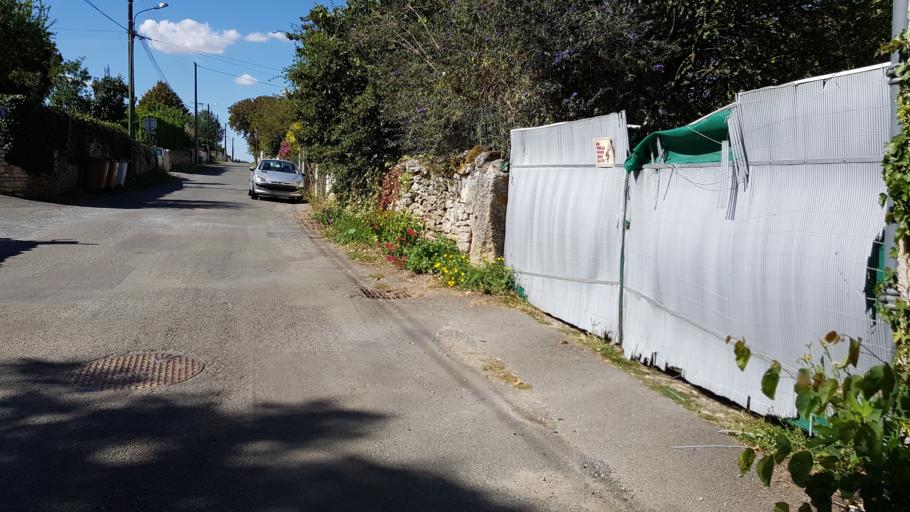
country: FR
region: Poitou-Charentes
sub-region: Departement des Deux-Sevres
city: Vouille
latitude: 46.3144
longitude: -0.3762
